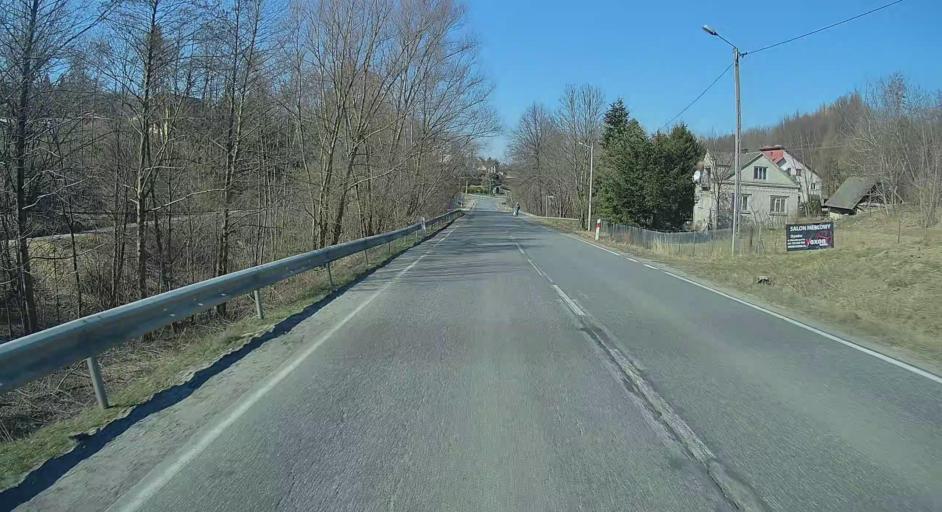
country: PL
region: Subcarpathian Voivodeship
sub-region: Powiat rzeszowski
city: Hyzne
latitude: 49.9022
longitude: 22.2119
